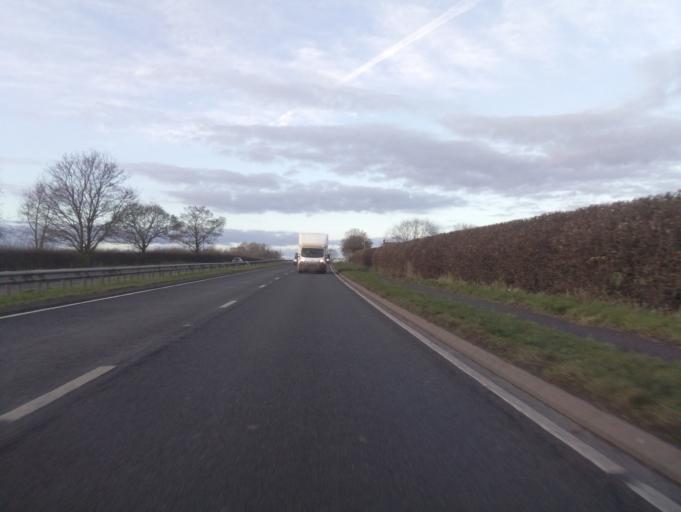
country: GB
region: England
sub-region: Staffordshire
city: Stafford
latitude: 52.8421
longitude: -2.1368
